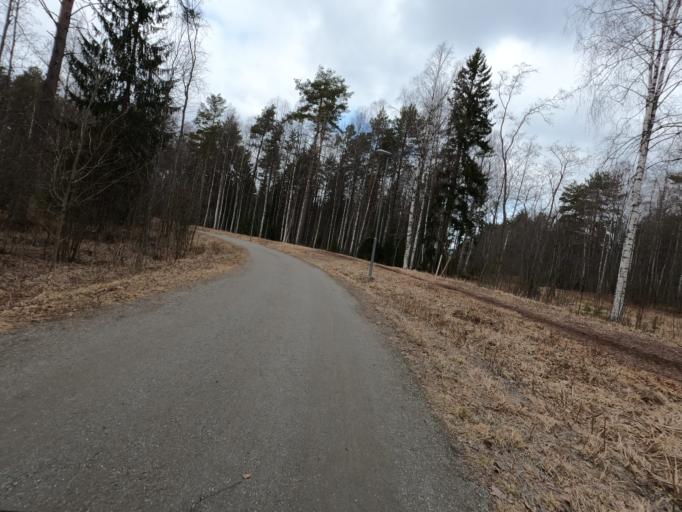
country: FI
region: North Karelia
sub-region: Joensuu
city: Joensuu
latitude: 62.5730
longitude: 29.8125
